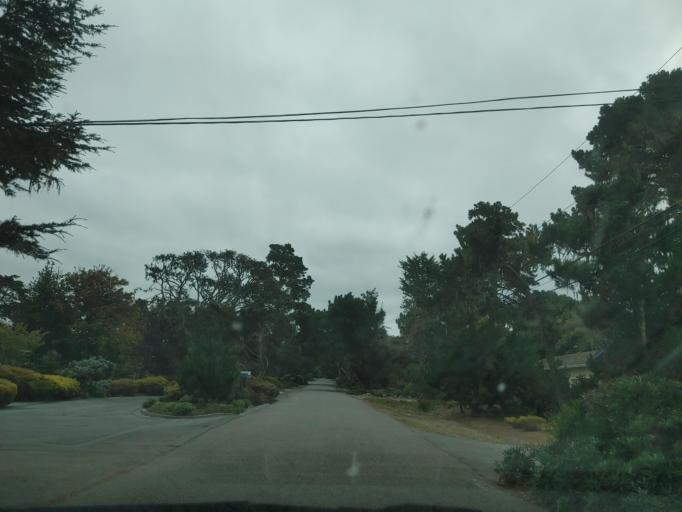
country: US
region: California
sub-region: Monterey County
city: Del Monte Forest
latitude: 36.6038
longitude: -121.9484
